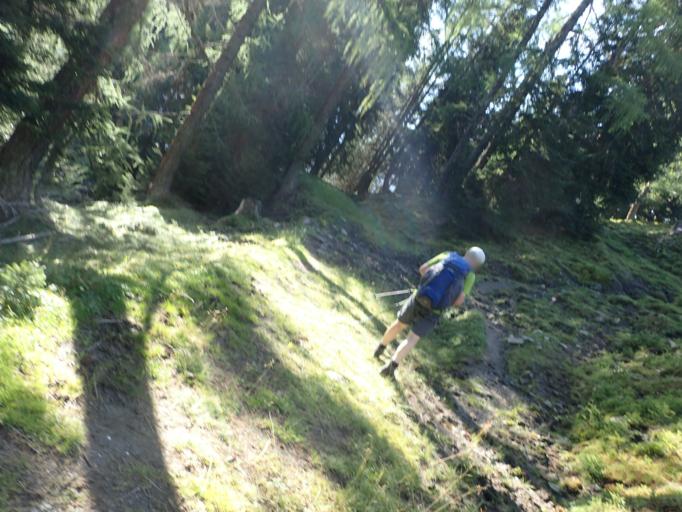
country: AT
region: Salzburg
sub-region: Politischer Bezirk Sankt Johann im Pongau
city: Huttschlag
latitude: 47.1471
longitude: 13.2296
